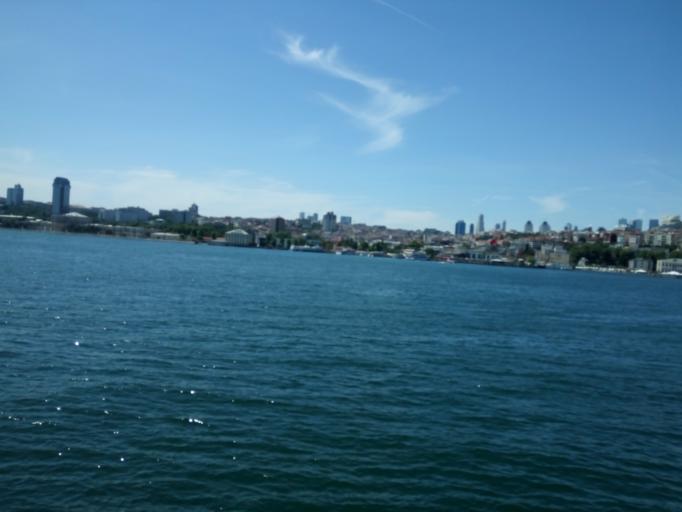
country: TR
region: Istanbul
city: UEskuedar
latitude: 41.0368
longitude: 29.0143
